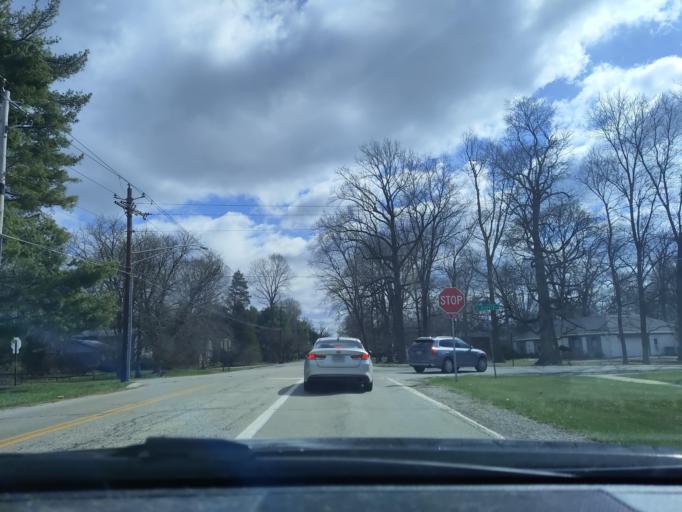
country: US
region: Indiana
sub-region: Marion County
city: Meridian Hills
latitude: 39.8976
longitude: -86.1749
